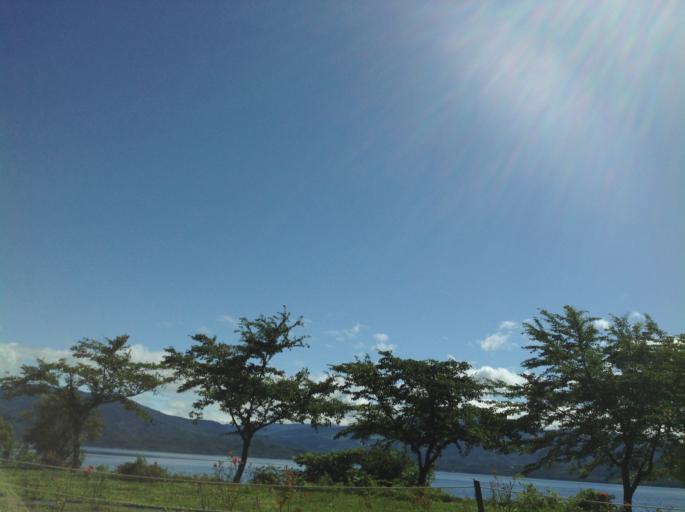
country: JP
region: Akita
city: Kakunodatemachi
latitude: 39.7116
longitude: 140.6342
